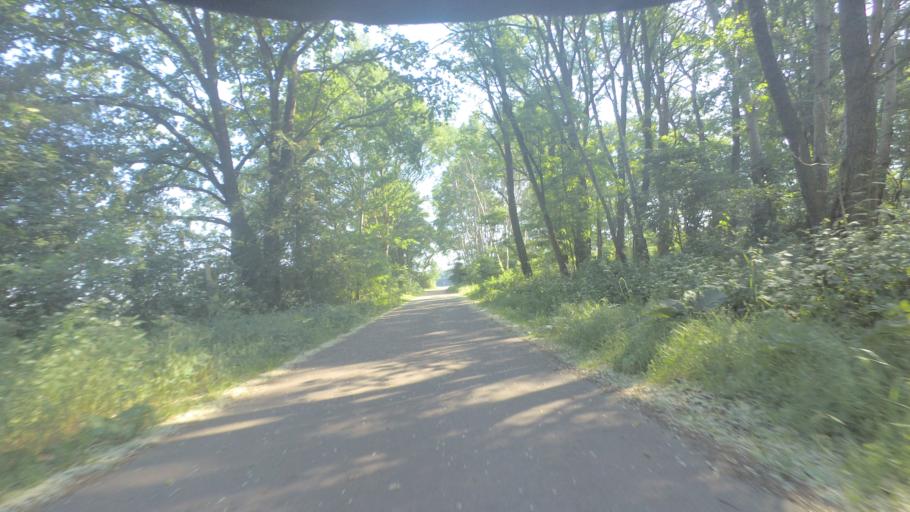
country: DE
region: Saxony-Anhalt
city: Quellendorf
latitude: 51.8228
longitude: 12.1593
